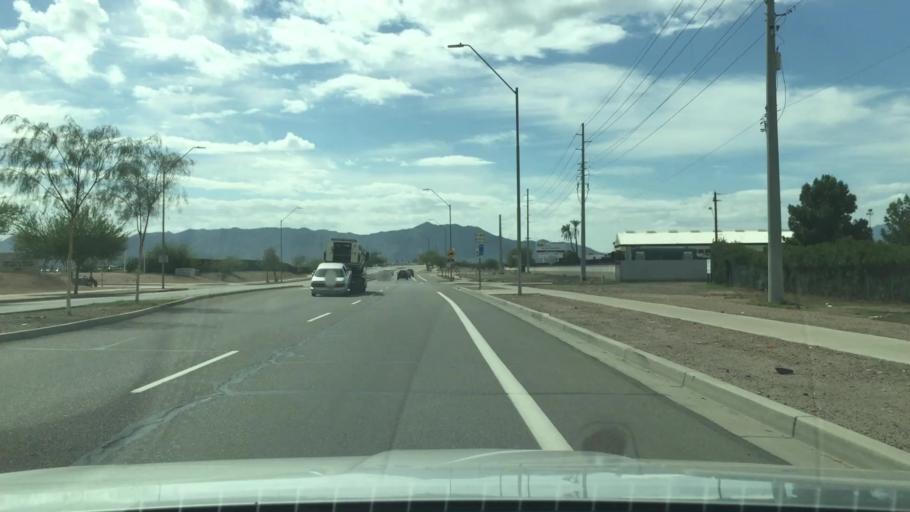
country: US
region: Arizona
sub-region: Maricopa County
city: Laveen
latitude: 33.4161
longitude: -112.1346
